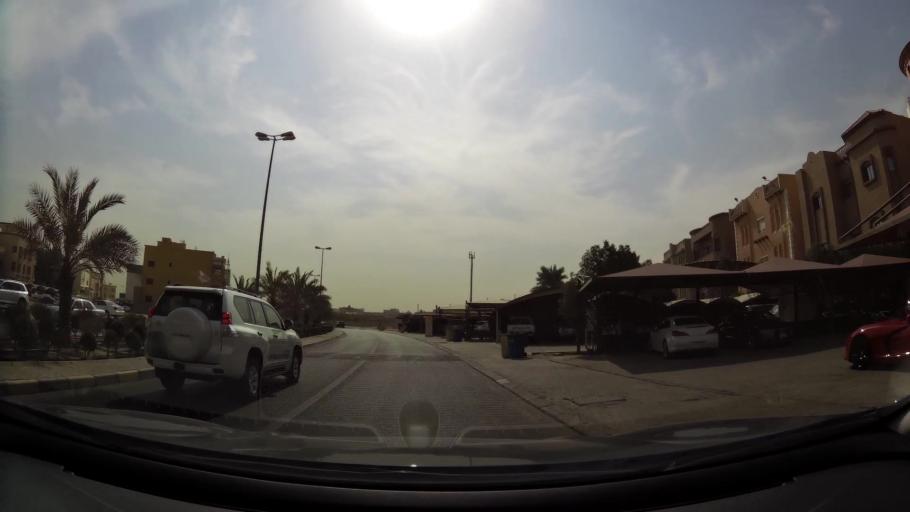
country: KW
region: Al Farwaniyah
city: Janub as Surrah
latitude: 29.2734
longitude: 47.9963
